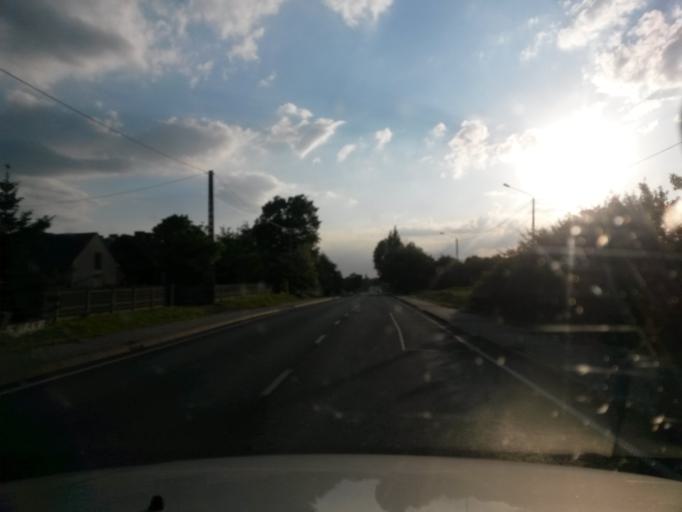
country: PL
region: Lodz Voivodeship
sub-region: Powiat wielunski
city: Wielun
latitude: 51.2294
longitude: 18.6182
